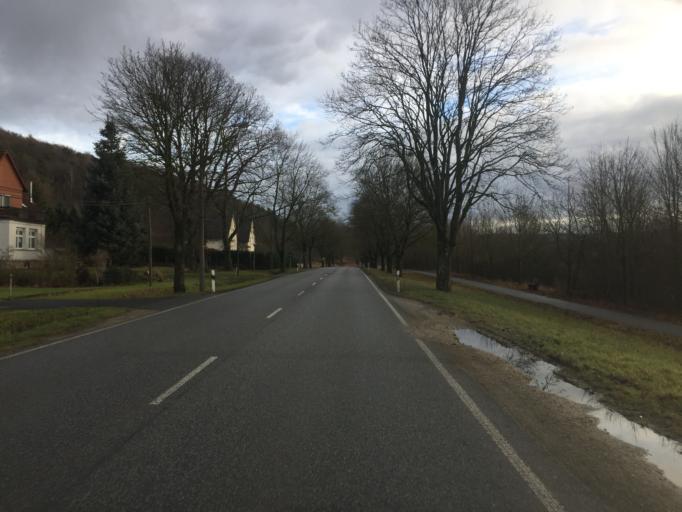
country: DE
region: Thuringia
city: Haynrode
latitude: 51.4135
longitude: 10.4616
